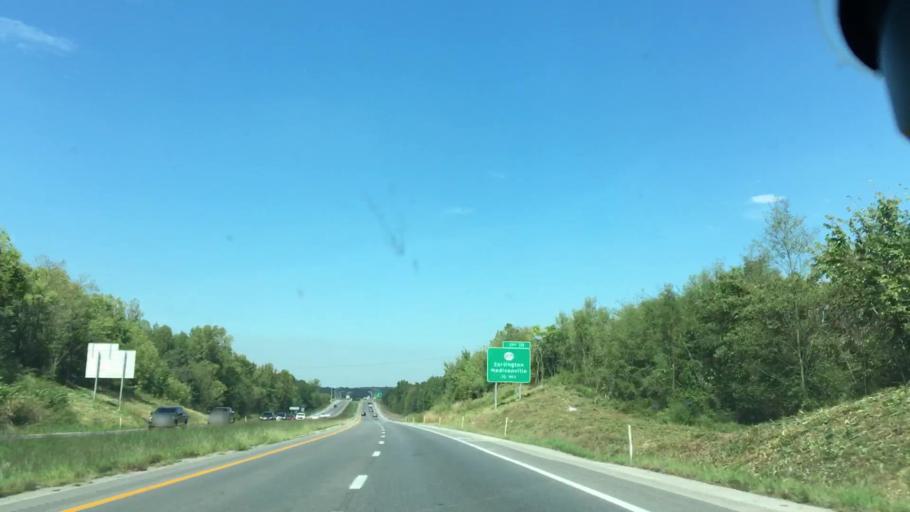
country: US
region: Kentucky
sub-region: Hopkins County
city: Earlington
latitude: 37.2843
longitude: -87.4575
